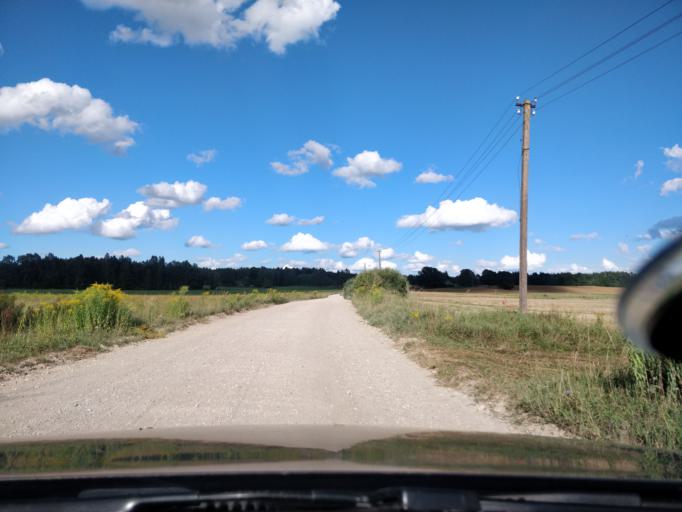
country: LV
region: Ogre
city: Ogre
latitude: 56.7953
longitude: 24.6524
